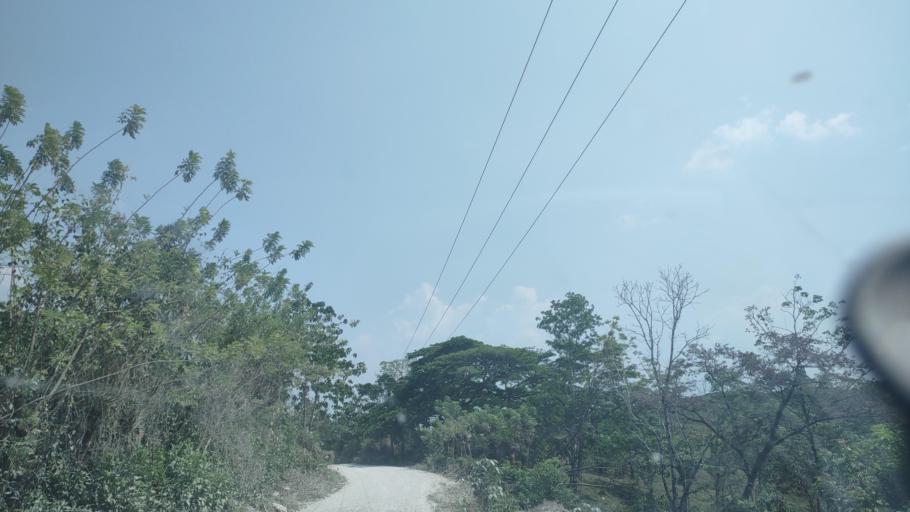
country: MX
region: Tabasco
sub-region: Huimanguillo
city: Francisco Rueda
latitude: 17.5749
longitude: -93.8891
